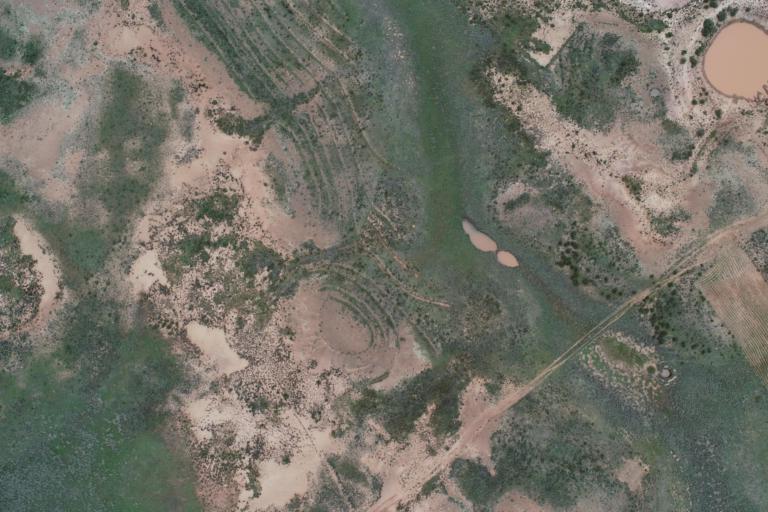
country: BO
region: La Paz
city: Curahuara de Carangas
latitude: -17.2930
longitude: -68.5091
